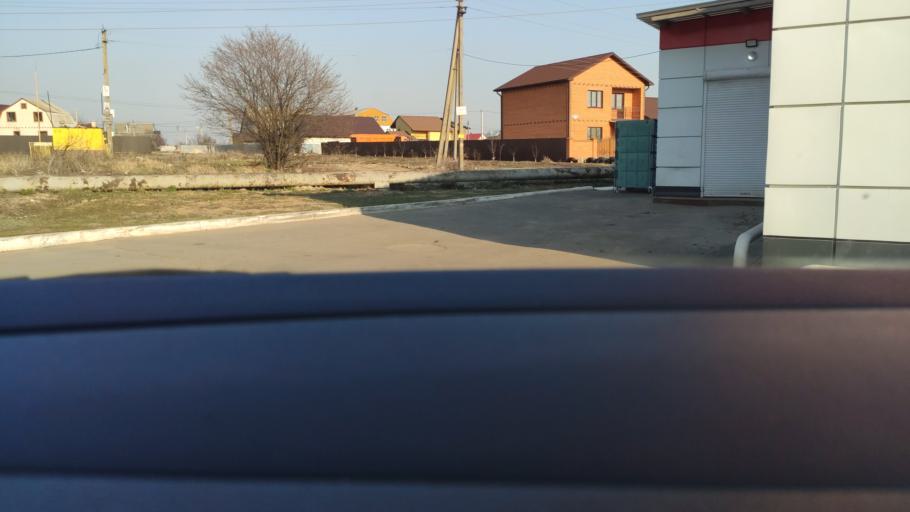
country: RU
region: Voronezj
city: Maslovka
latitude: 51.5846
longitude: 39.3200
